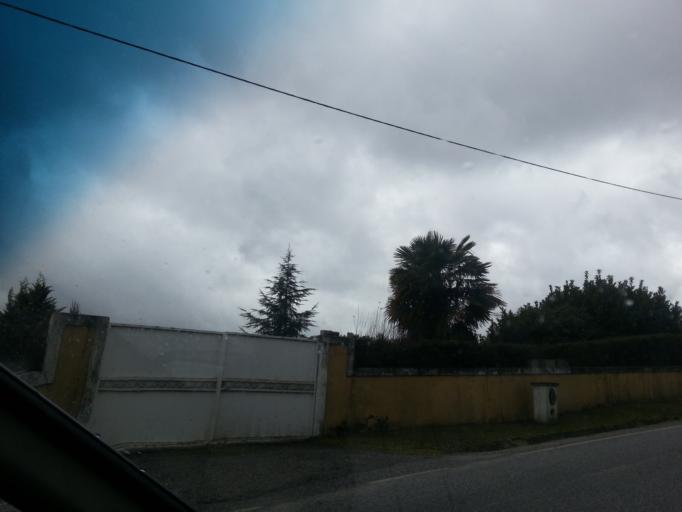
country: PT
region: Viseu
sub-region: Viseu
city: Rio de Loba
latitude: 40.6213
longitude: -7.8675
